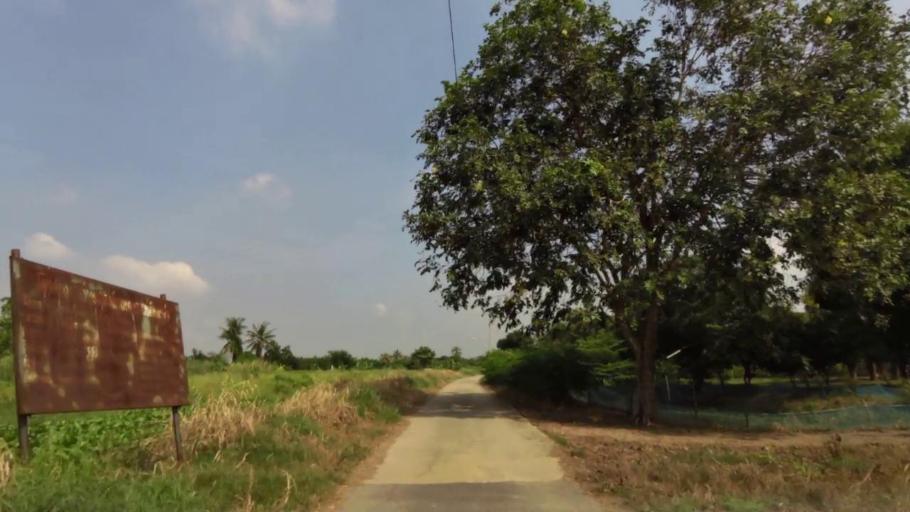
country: TH
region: Ang Thong
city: Wiset Chaichan
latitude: 14.6099
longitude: 100.3932
